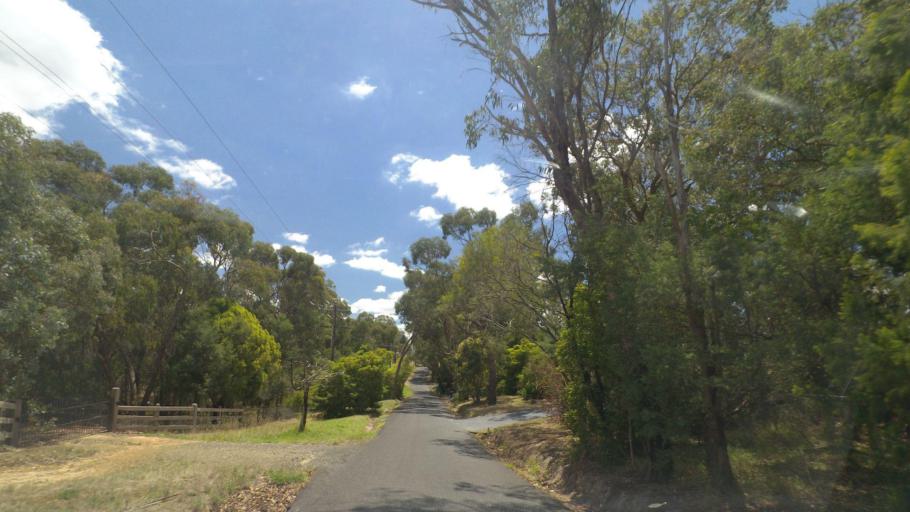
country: AU
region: Victoria
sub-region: Manningham
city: Warrandyte
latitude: -37.7319
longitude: 145.2650
